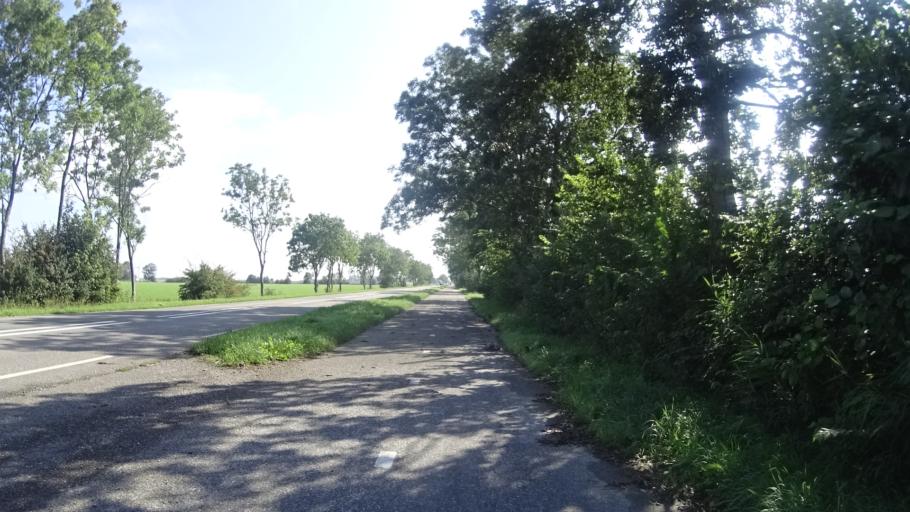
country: NL
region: Friesland
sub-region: Menameradiel
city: Dronryp
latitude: 53.1960
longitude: 5.6189
